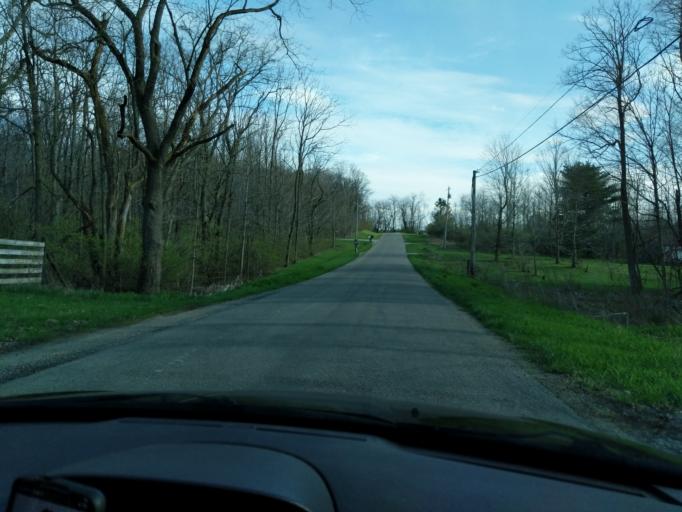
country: US
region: Ohio
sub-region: Champaign County
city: North Lewisburg
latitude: 40.1863
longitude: -83.6443
